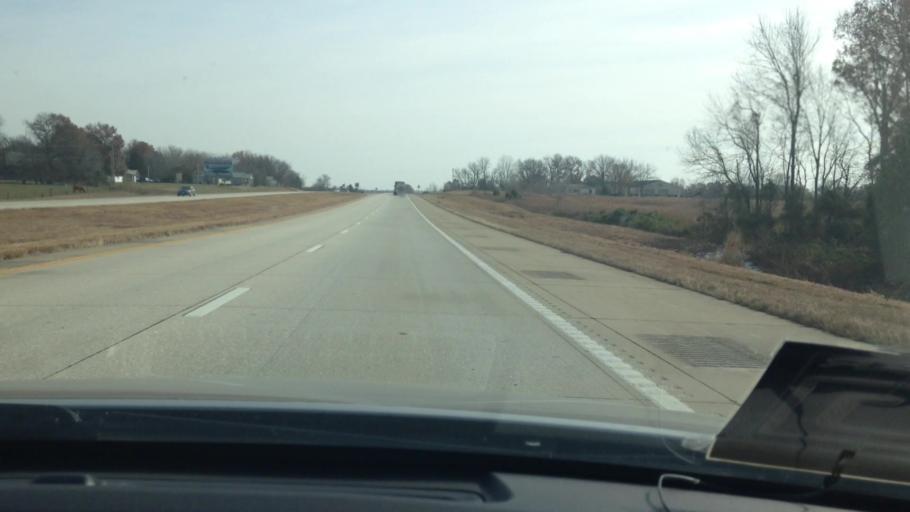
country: US
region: Missouri
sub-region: Henry County
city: Clinton
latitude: 38.4363
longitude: -93.9397
